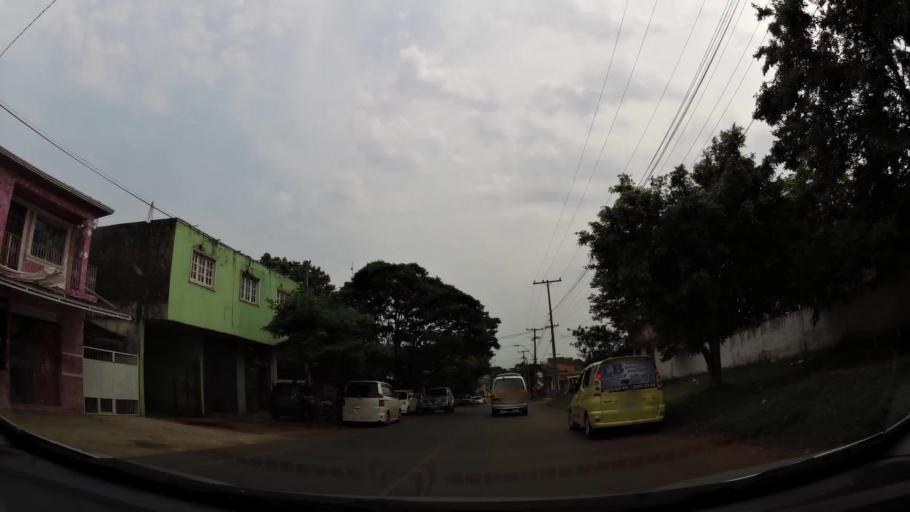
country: BR
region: Parana
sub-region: Foz Do Iguacu
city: Foz do Iguacu
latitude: -25.5629
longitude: -54.6043
